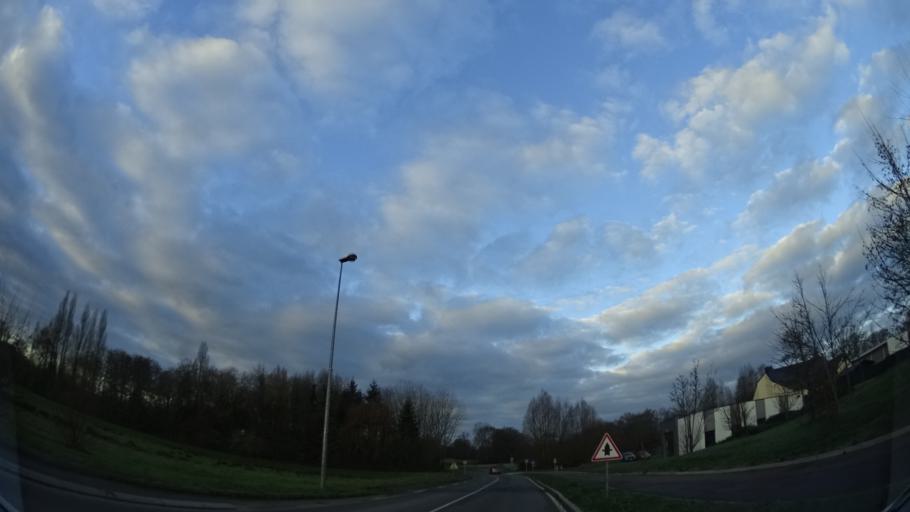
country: FR
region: Brittany
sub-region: Departement d'Ille-et-Vilaine
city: Betton
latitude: 48.1751
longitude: -1.6629
